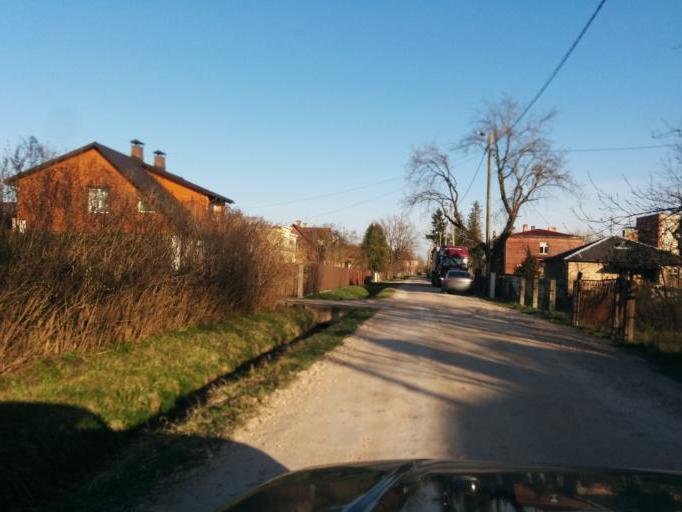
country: LV
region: Jelgava
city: Jelgava
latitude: 56.6554
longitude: 23.7445
